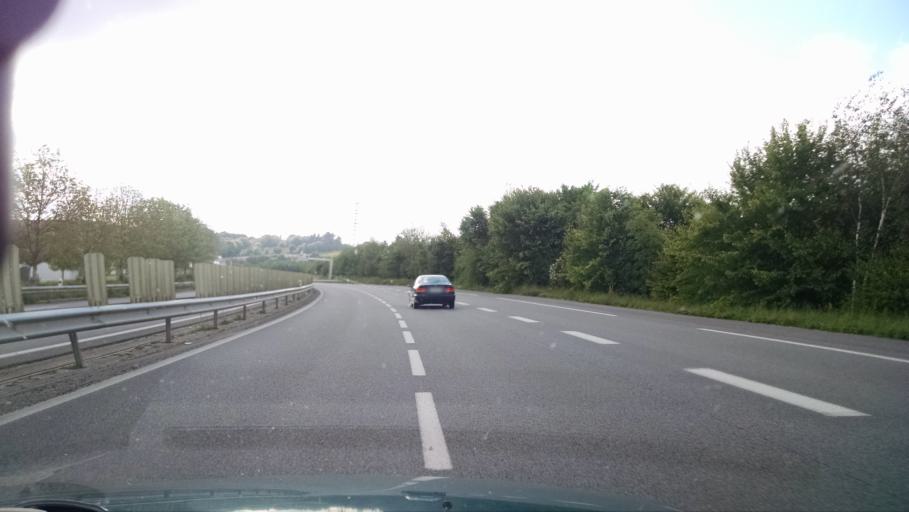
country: FR
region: Brittany
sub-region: Departement du Finistere
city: Morlaix
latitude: 48.5814
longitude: -3.8654
